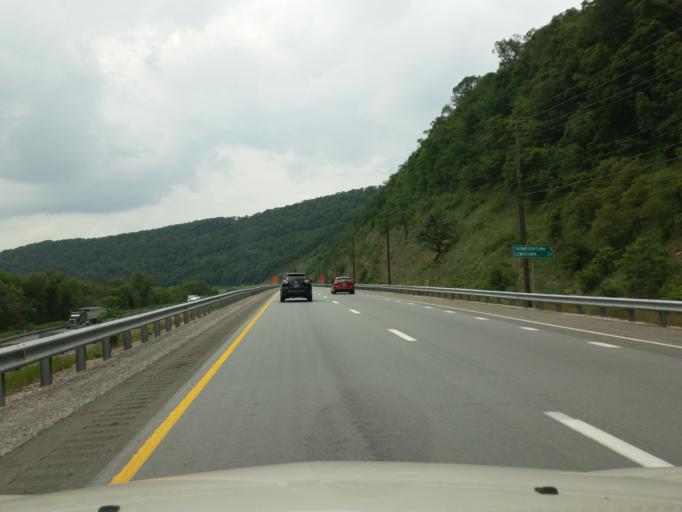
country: US
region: Pennsylvania
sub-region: Perry County
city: Newport
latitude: 40.5590
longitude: -77.1636
